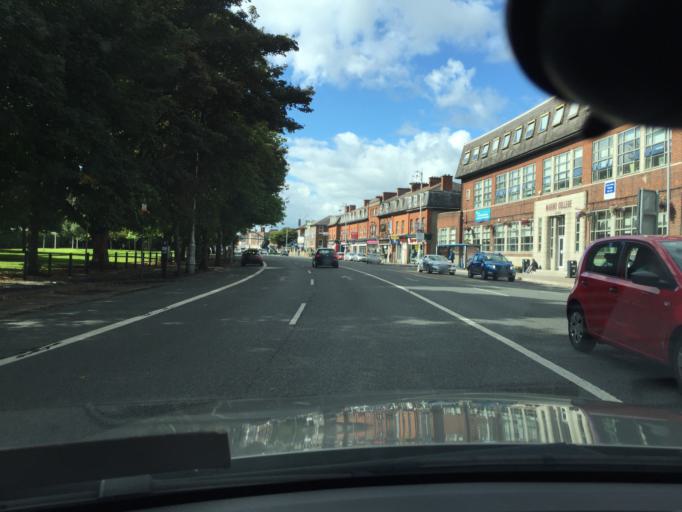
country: IE
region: Leinster
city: Marino
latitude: 53.3643
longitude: -6.2306
